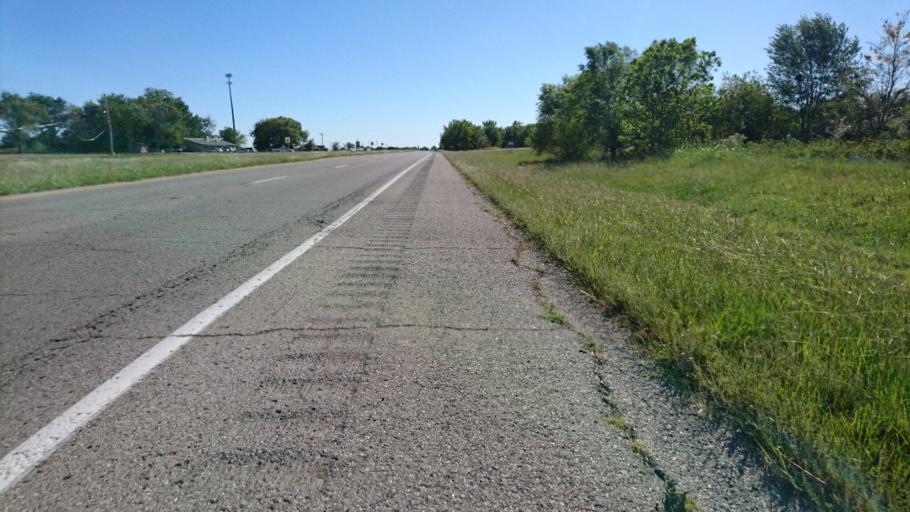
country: US
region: Oklahoma
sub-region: Rogers County
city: Justice
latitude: 36.3841
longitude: -95.5560
